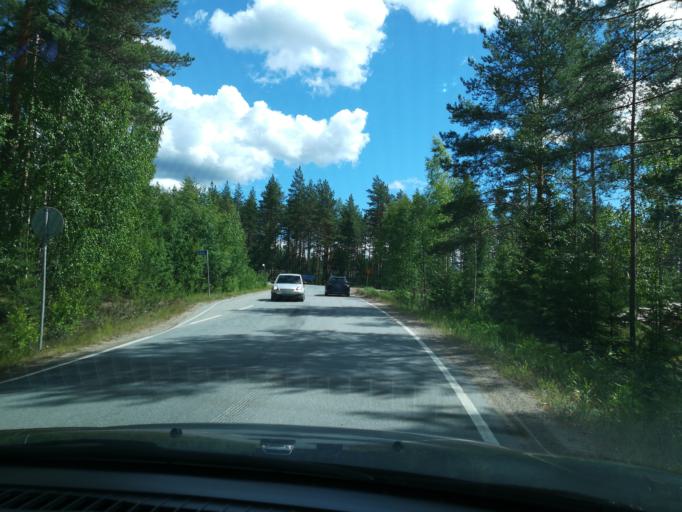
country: FI
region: Southern Savonia
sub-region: Mikkeli
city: Hirvensalmi
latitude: 61.6201
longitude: 26.7802
